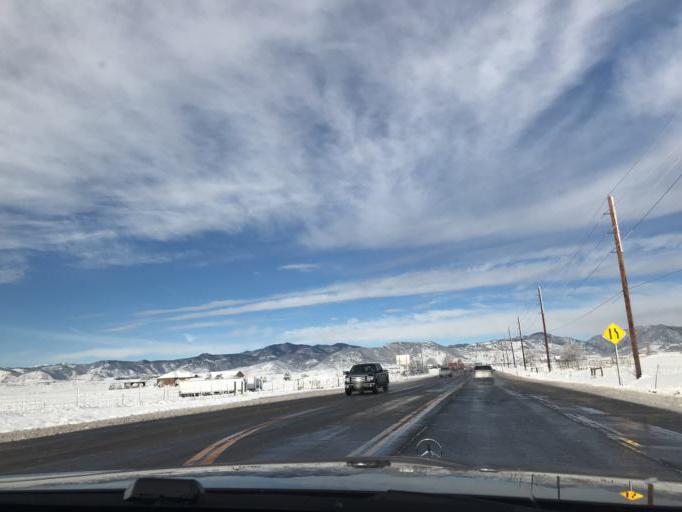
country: US
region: Colorado
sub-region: Jefferson County
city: Arvada
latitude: 39.8508
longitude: -105.1661
